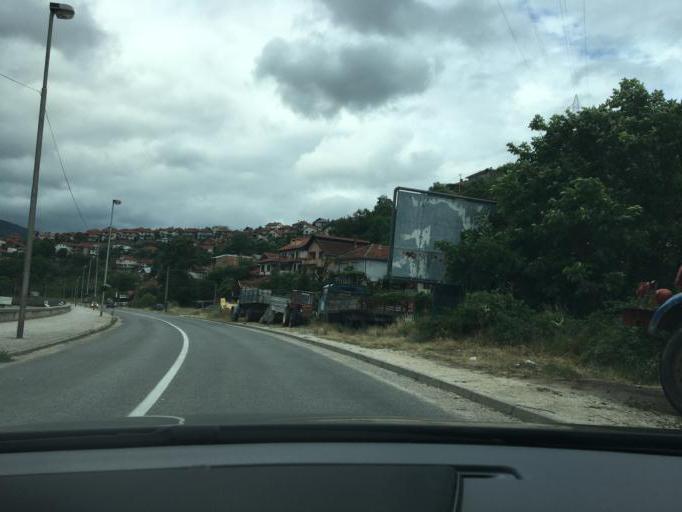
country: MK
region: Kriva Palanka
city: Kriva Palanka
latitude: 42.2075
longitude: 22.3357
